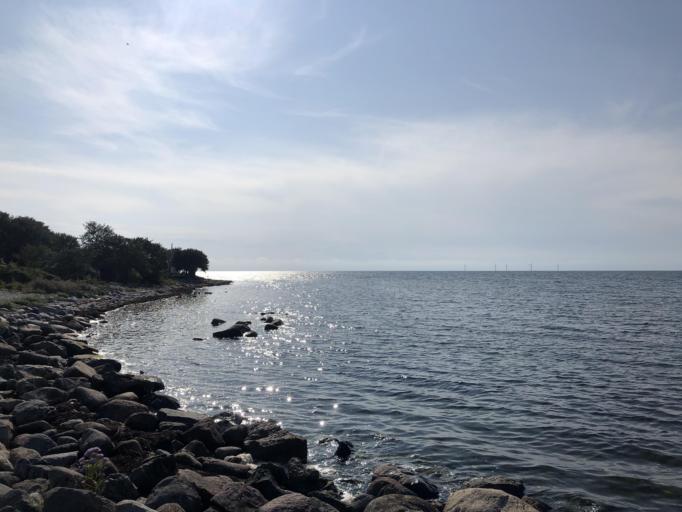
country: SE
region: Gotland
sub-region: Gotland
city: Hemse
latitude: 57.0313
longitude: 18.2205
